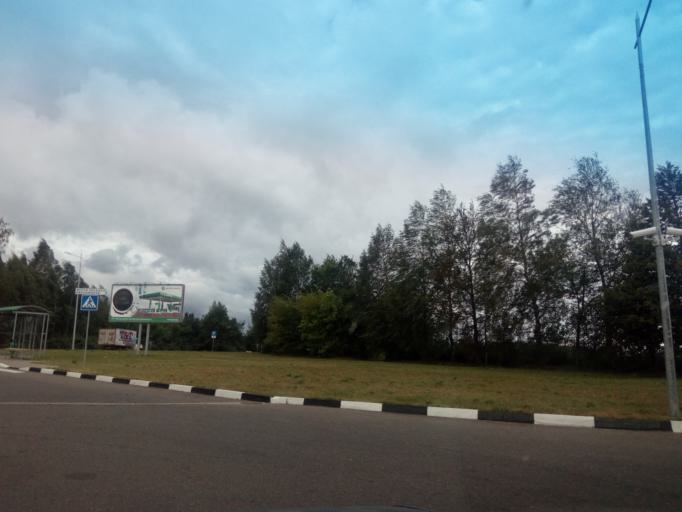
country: BY
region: Vitebsk
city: Polatsk
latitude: 55.5048
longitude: 28.7391
